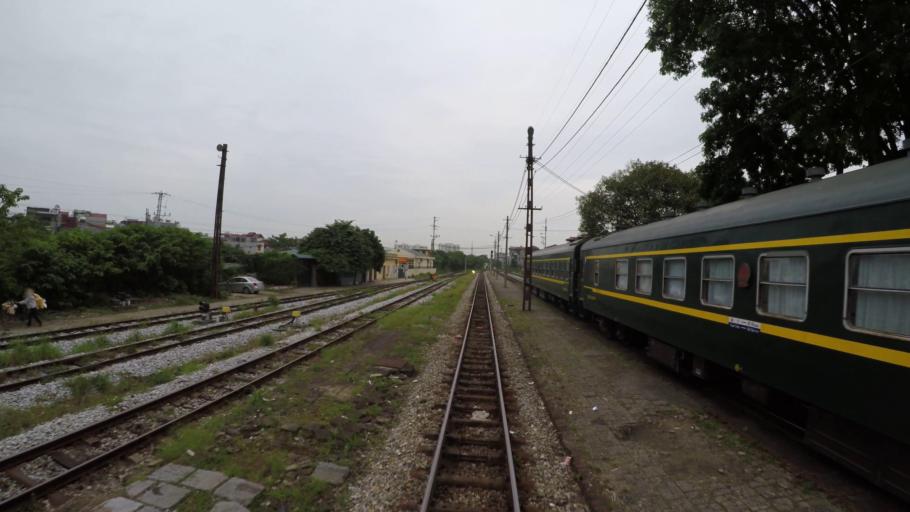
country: VN
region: Ha Noi
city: Trau Quy
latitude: 21.0254
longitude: 105.9262
